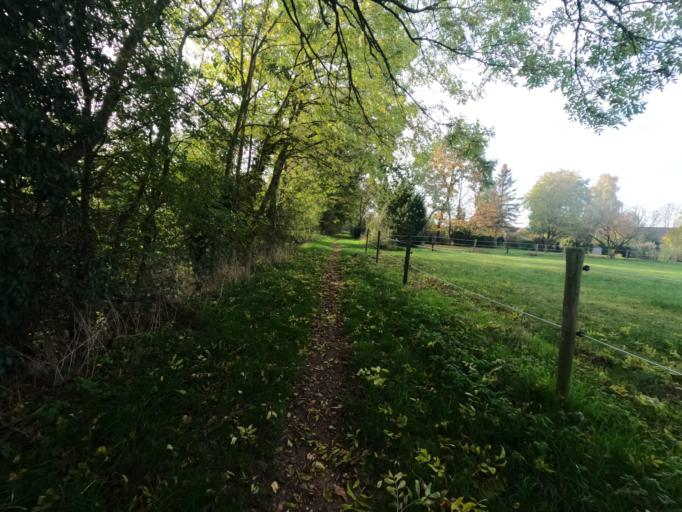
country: DE
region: North Rhine-Westphalia
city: Erkelenz
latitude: 51.0535
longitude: 6.3165
